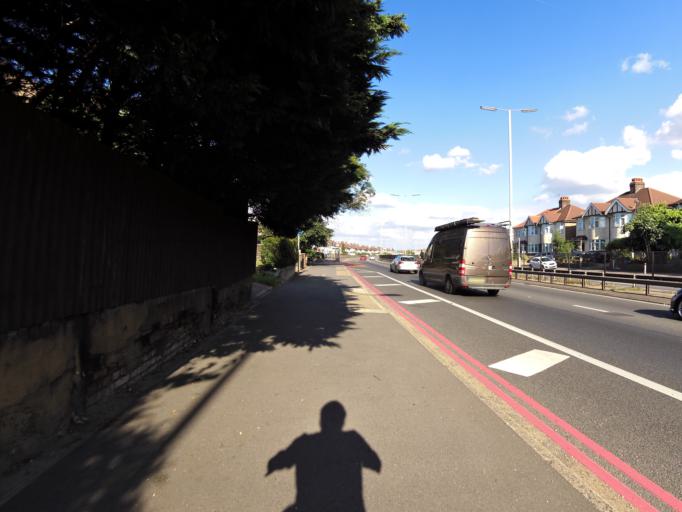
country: GB
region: England
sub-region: Greater London
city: Wood Green
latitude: 51.6156
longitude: -0.0986
